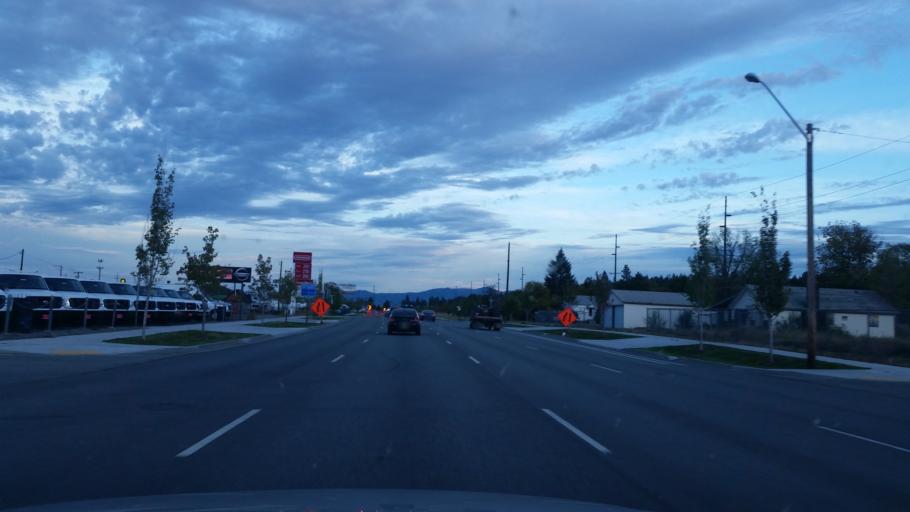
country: US
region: Washington
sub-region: Spokane County
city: Dishman
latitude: 47.6560
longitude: -117.3111
